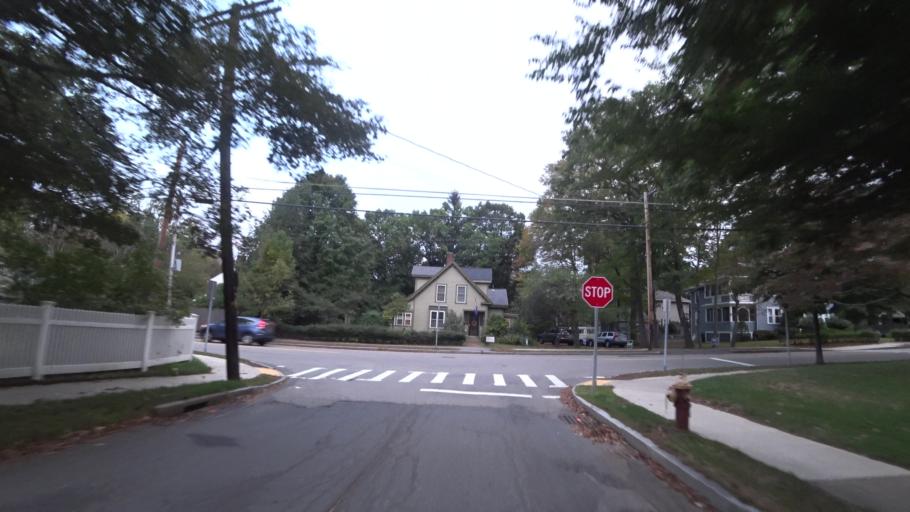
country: US
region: Massachusetts
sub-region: Middlesex County
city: Newton
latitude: 42.3222
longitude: -71.1939
